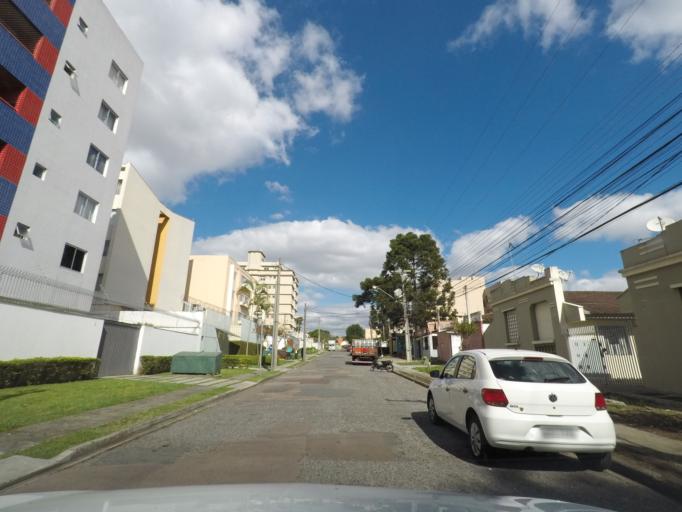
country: BR
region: Parana
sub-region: Curitiba
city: Curitiba
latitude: -25.4377
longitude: -49.2479
